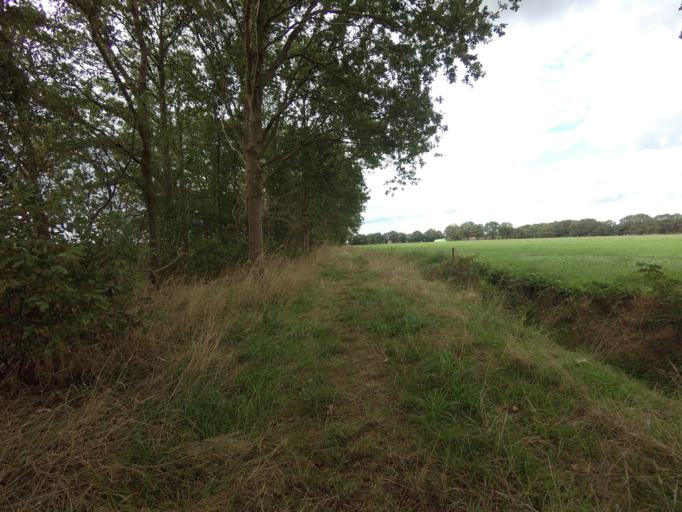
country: NL
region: Friesland
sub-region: Gemeente Heerenveen
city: Jubbega
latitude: 52.9619
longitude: 6.1850
